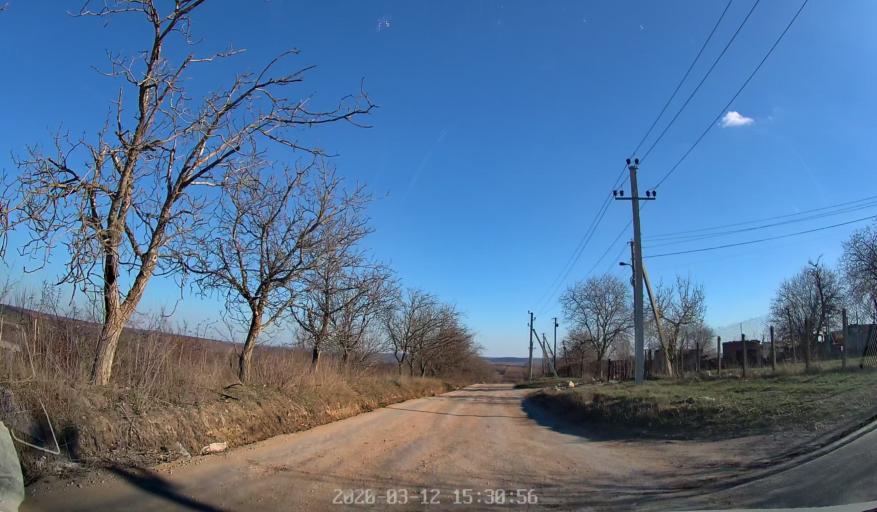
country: MD
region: Chisinau
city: Ciorescu
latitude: 47.1591
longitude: 28.9408
